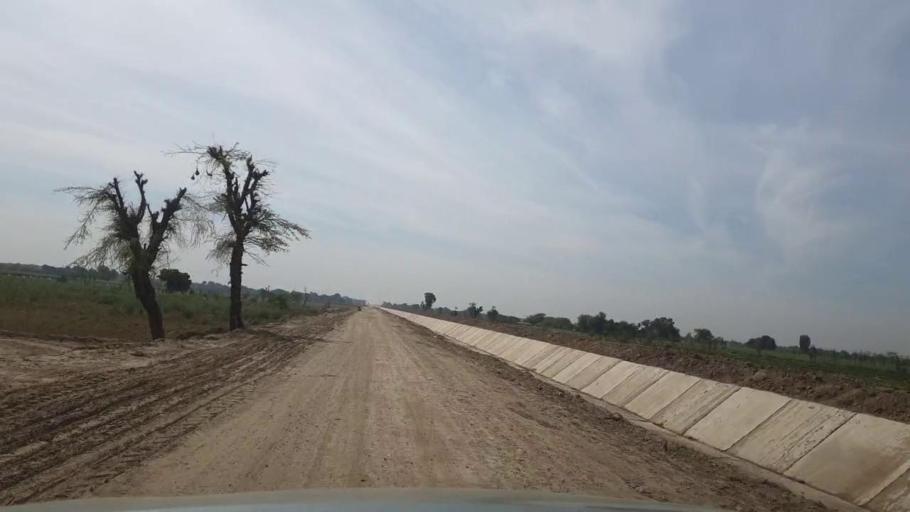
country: PK
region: Sindh
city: Kunri
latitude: 25.1558
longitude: 69.5893
